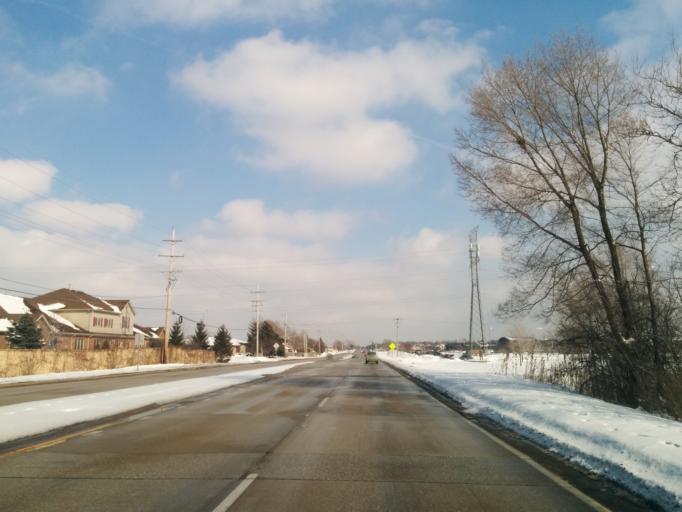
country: US
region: Illinois
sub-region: Cook County
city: Orland Hills
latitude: 41.5799
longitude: -87.8206
